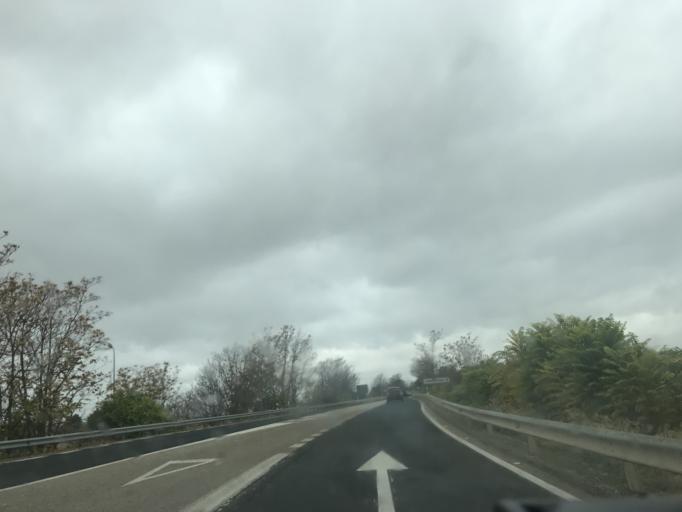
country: ES
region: Andalusia
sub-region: Provincia de Jaen
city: Peal de Becerro
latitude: 37.9147
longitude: -3.1048
